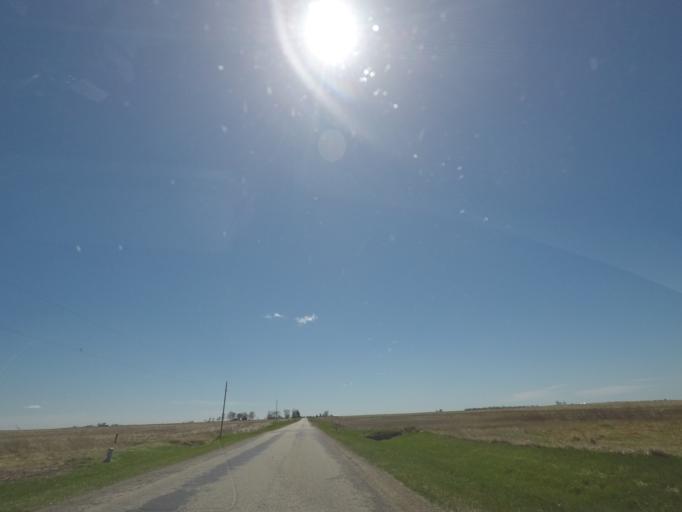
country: US
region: Illinois
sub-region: Logan County
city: Atlanta
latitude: 40.1778
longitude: -89.1940
